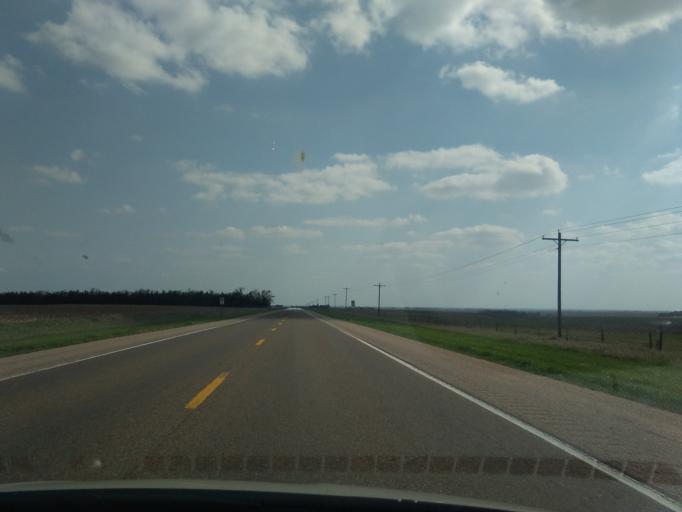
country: US
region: Nebraska
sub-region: Nuckolls County
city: Nelson
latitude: 40.1171
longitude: -98.0670
